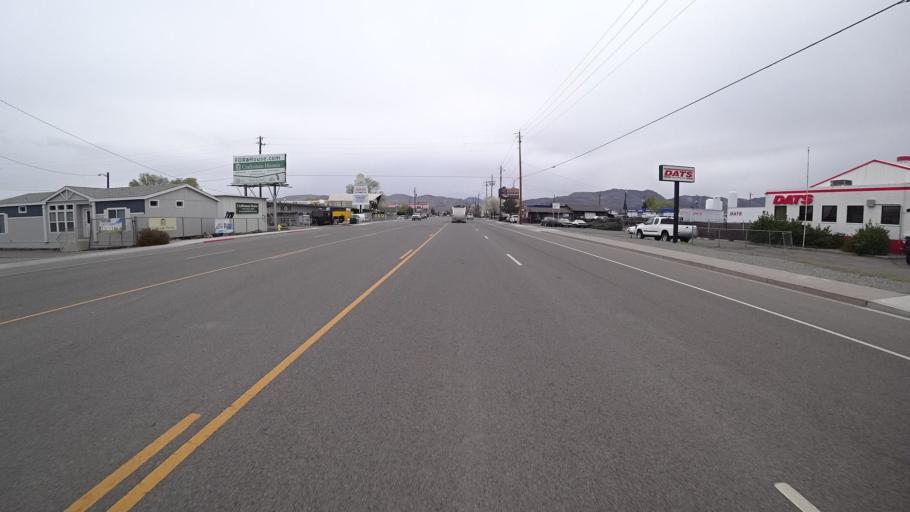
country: US
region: Nevada
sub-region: Washoe County
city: Sparks
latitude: 39.5277
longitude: -119.7558
